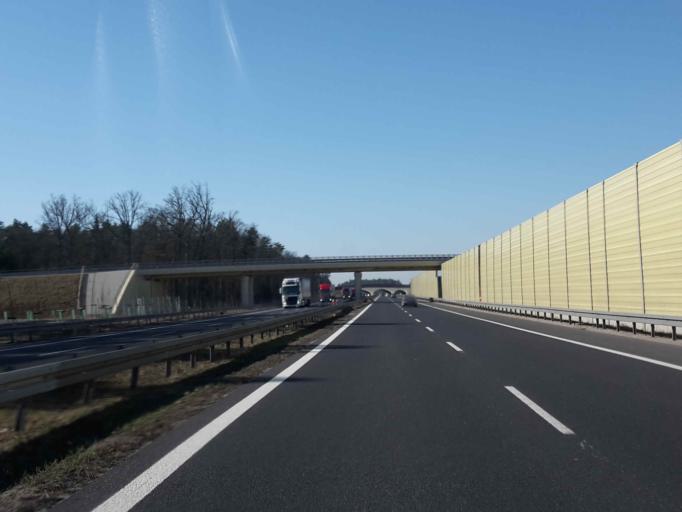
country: PL
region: Greater Poland Voivodeship
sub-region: Powiat poznanski
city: Pobiedziska
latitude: 52.4442
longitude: 17.3555
